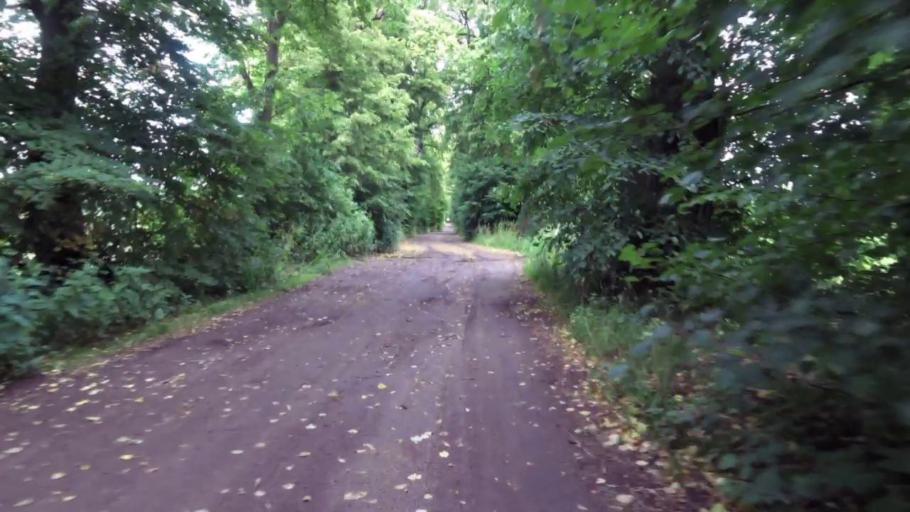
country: PL
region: West Pomeranian Voivodeship
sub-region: Powiat pyrzycki
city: Lipiany
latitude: 52.9694
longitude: 14.9284
